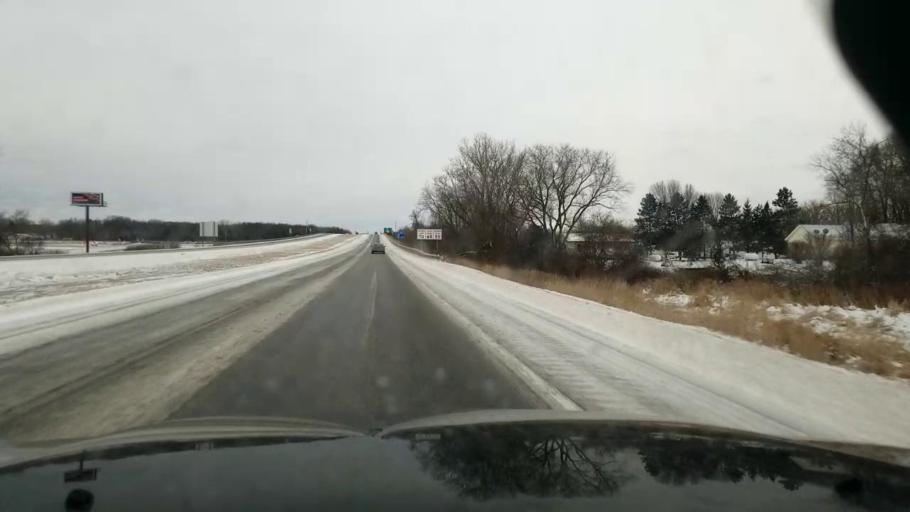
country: US
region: Michigan
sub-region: Jackson County
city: Jackson
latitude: 42.2606
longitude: -84.4768
